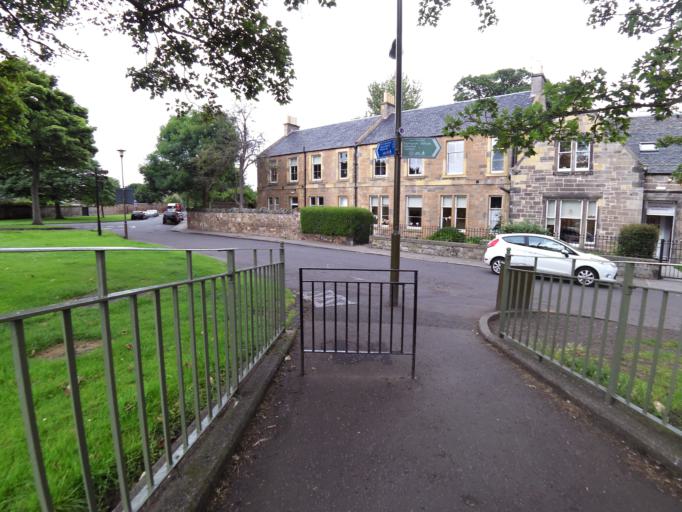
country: GB
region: Scotland
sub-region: East Lothian
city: Musselburgh
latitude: 55.9455
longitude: -3.0504
